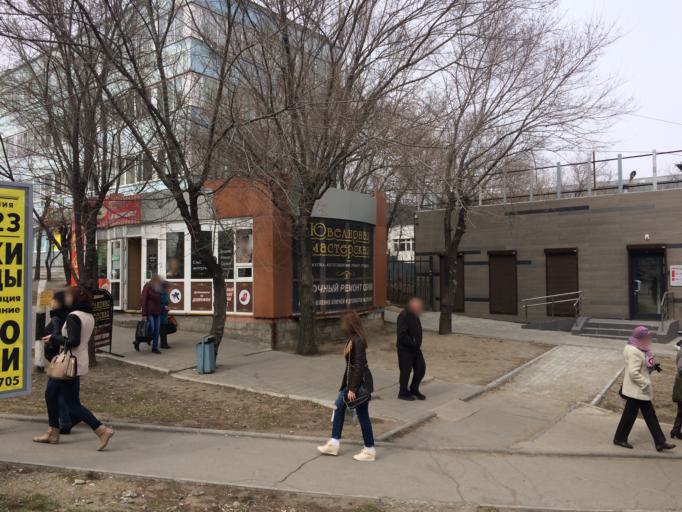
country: RU
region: Khabarovsk Krai
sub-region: Khabarovskiy Rayon
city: Khabarovsk
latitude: 48.4832
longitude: 135.0943
